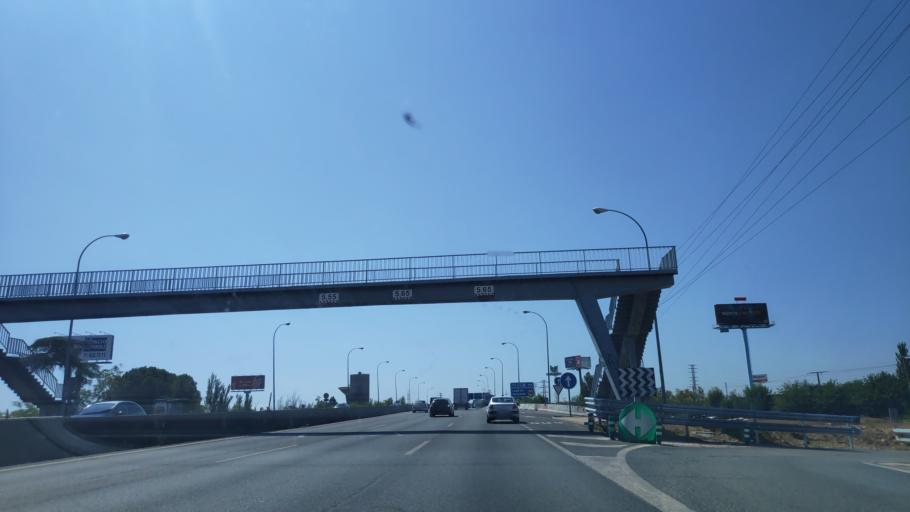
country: ES
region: Madrid
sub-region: Provincia de Madrid
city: Villaverde
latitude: 40.3448
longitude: -3.7236
